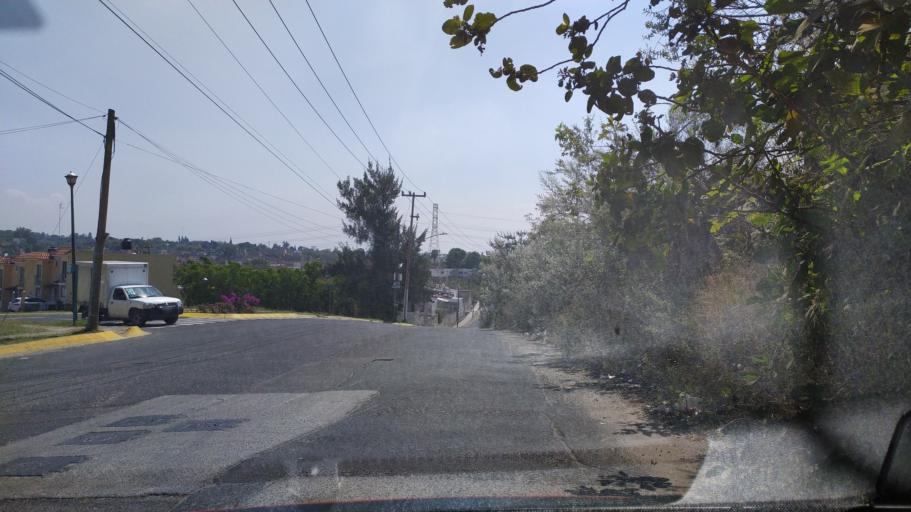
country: MX
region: Jalisco
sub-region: Zapopan
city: Campo Real
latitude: 20.7737
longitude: -103.4341
